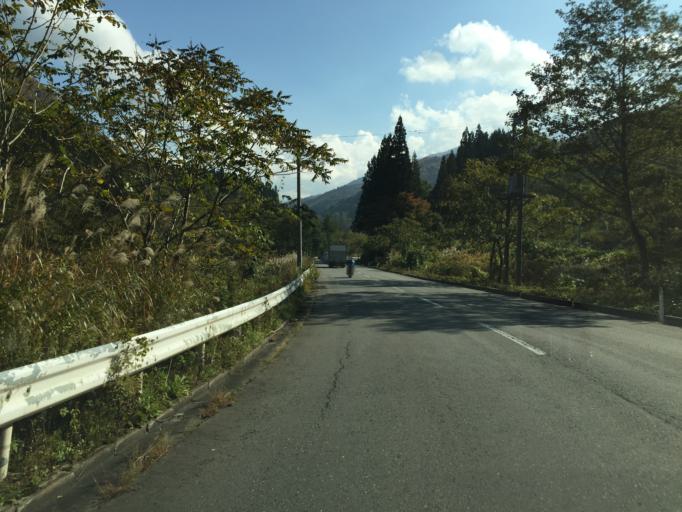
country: JP
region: Yamagata
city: Yonezawa
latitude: 37.8686
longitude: 139.9836
